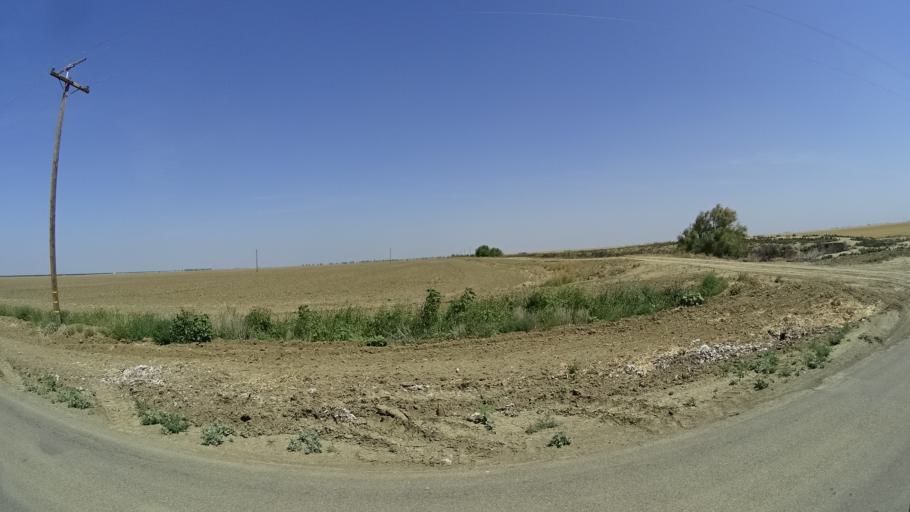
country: US
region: California
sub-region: Kings County
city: Stratford
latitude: 36.1377
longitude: -119.9241
